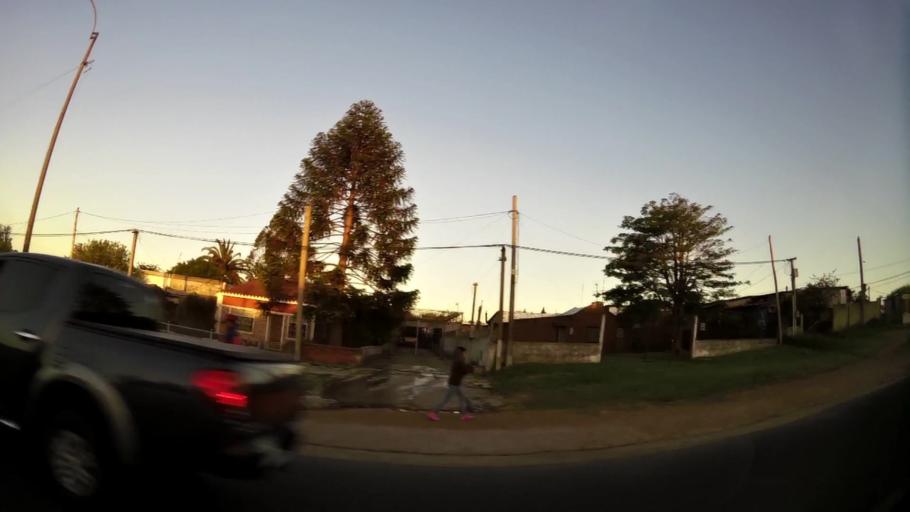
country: UY
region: Montevideo
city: Montevideo
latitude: -34.8266
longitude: -56.1684
